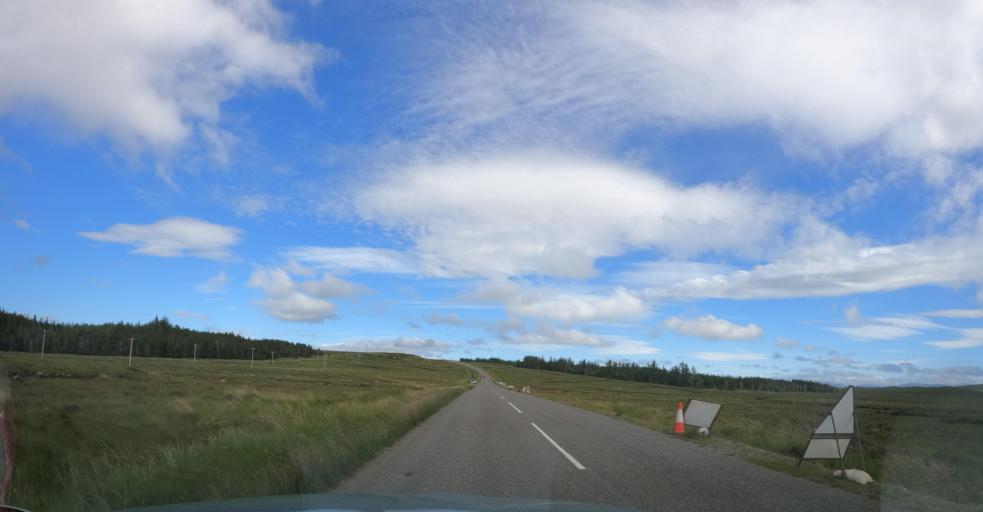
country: GB
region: Scotland
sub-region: Eilean Siar
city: Isle of Lewis
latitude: 58.1823
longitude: -6.6667
